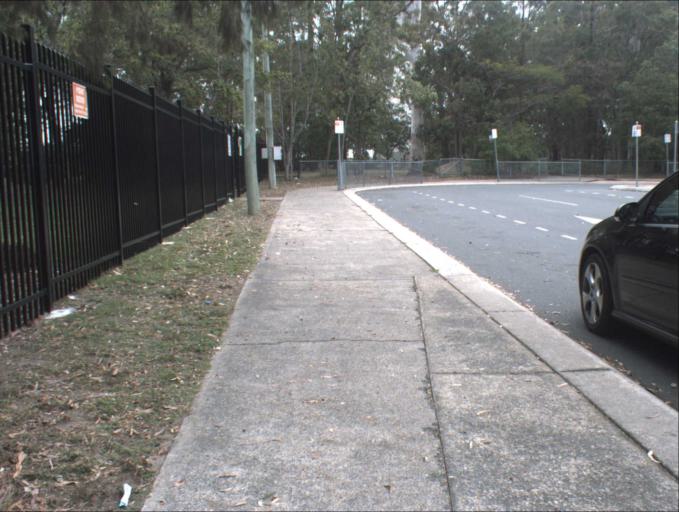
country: AU
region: Queensland
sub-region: Logan
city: Park Ridge South
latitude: -27.6843
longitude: 153.0178
